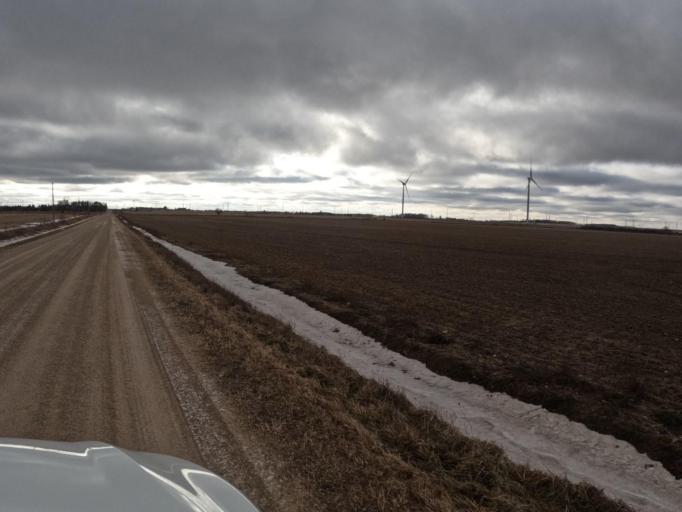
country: CA
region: Ontario
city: Shelburne
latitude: 44.0149
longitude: -80.3904
